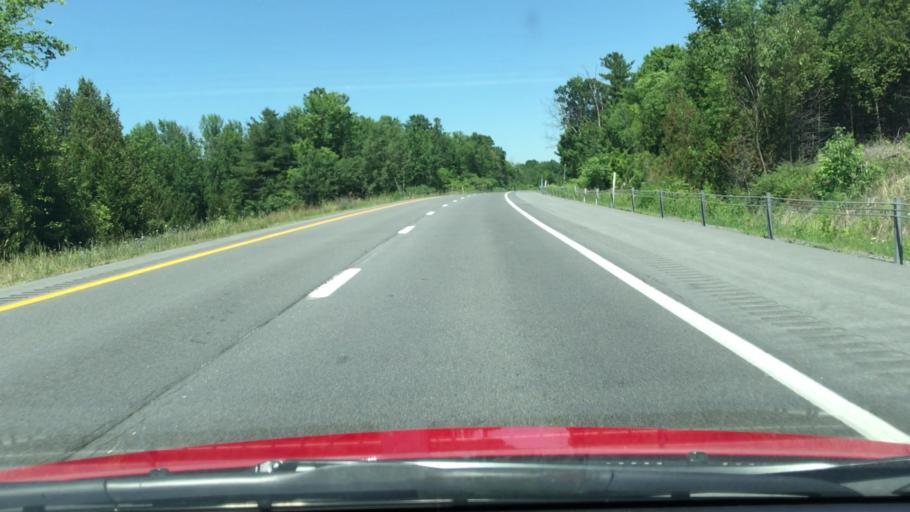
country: US
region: New York
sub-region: Clinton County
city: Champlain
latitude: 44.8713
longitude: -73.4514
